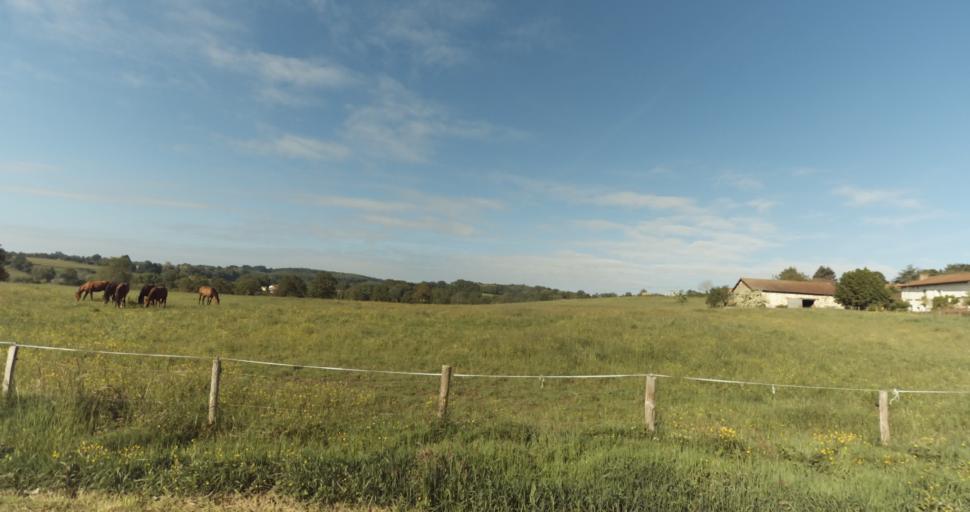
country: FR
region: Limousin
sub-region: Departement de la Haute-Vienne
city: Solignac
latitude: 45.7430
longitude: 1.2757
